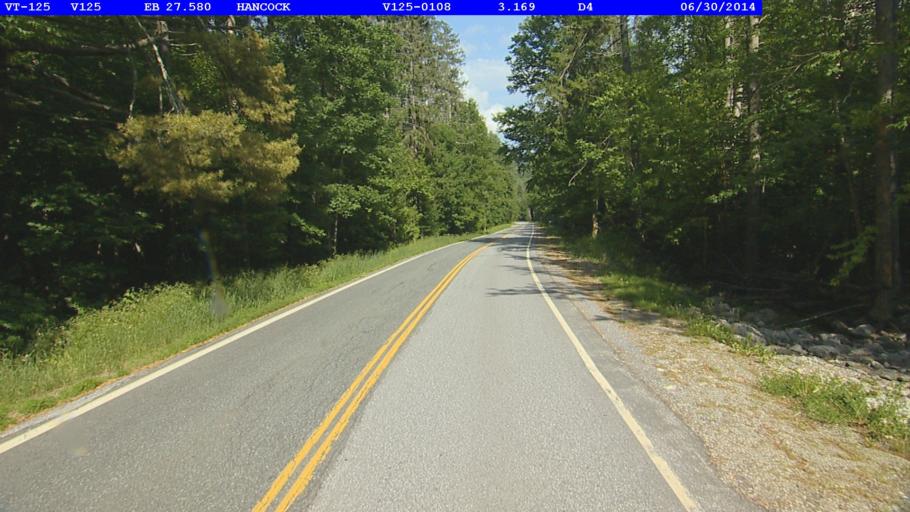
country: US
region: Vermont
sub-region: Rutland County
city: Brandon
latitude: 43.9275
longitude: -72.9191
